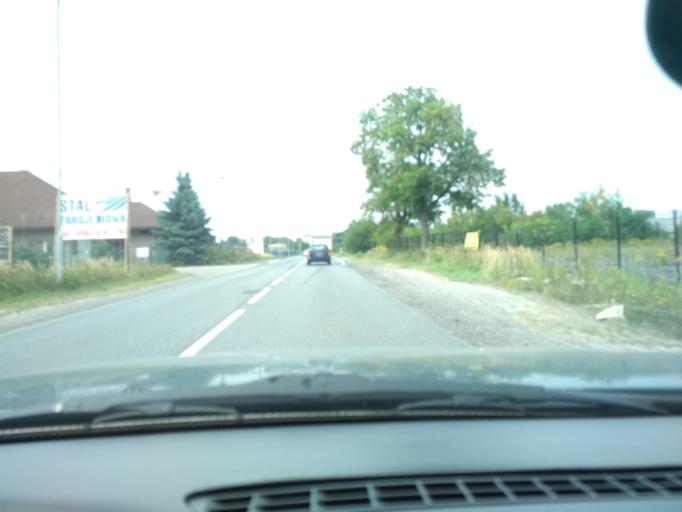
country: PL
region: Silesian Voivodeship
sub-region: Powiat zawiercianski
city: Zawiercie
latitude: 50.4732
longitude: 19.4052
